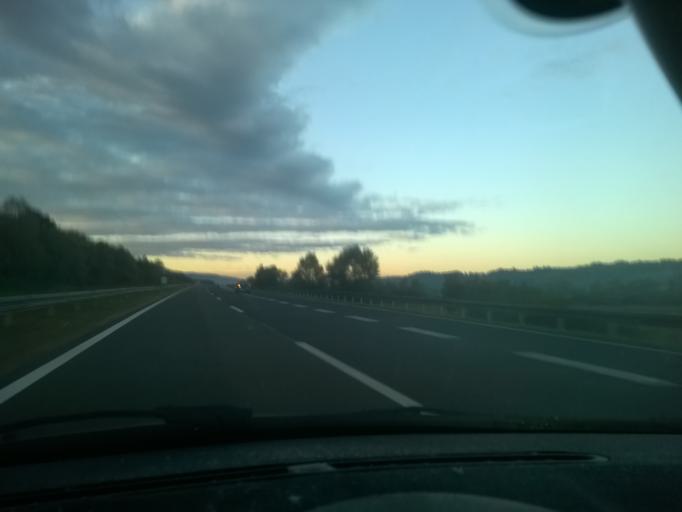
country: HR
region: Krapinsko-Zagorska
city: Zabok
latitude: 46.0646
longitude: 15.9196
